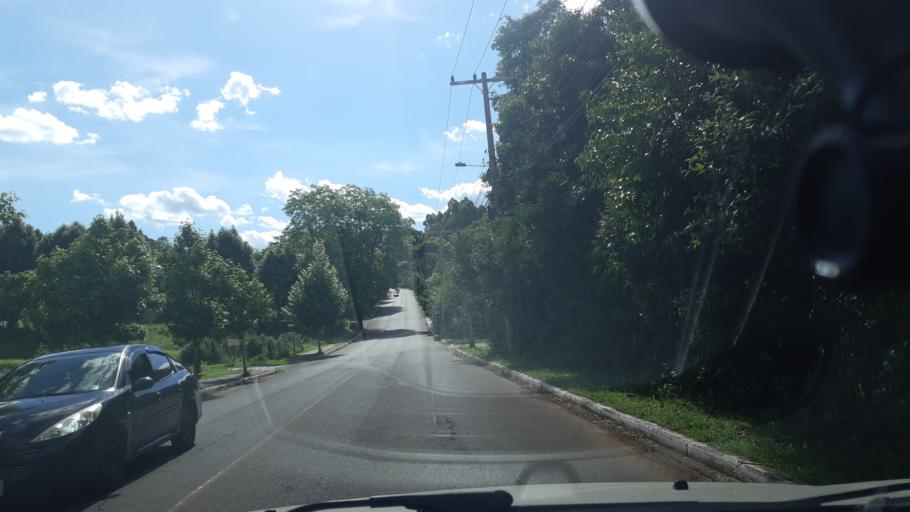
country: BR
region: Rio Grande do Sul
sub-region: Ivoti
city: Ivoti
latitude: -29.6195
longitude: -51.1166
